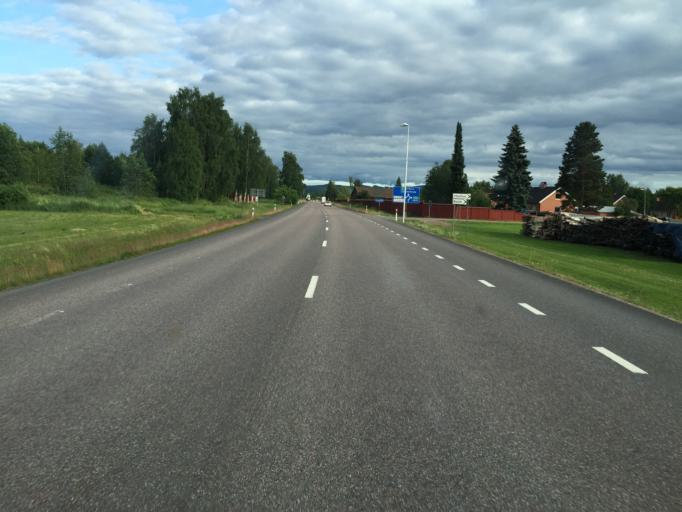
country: SE
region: Dalarna
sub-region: Gagnefs Kommun
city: Djuras
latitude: 60.5660
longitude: 15.1275
